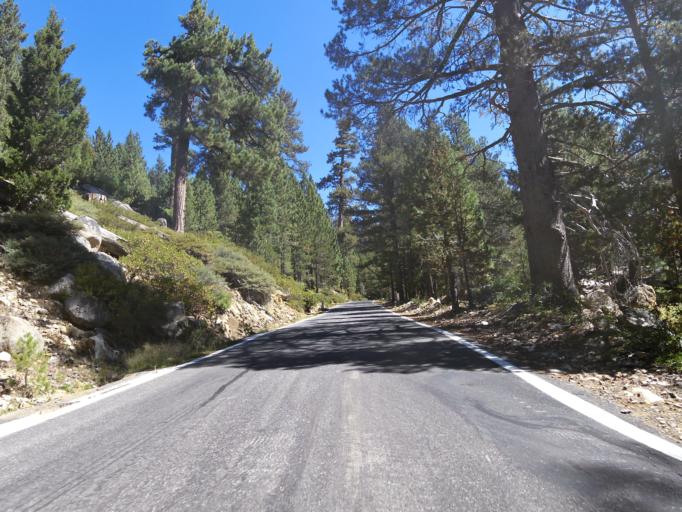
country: US
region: Nevada
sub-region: Douglas County
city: Gardnerville Ranchos
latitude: 38.5479
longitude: -119.8653
